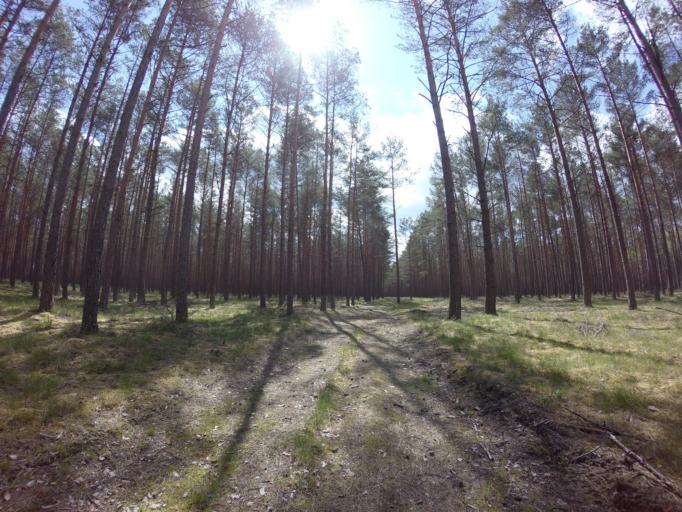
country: PL
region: West Pomeranian Voivodeship
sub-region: Powiat drawski
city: Kalisz Pomorski
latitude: 53.1982
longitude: 15.9796
